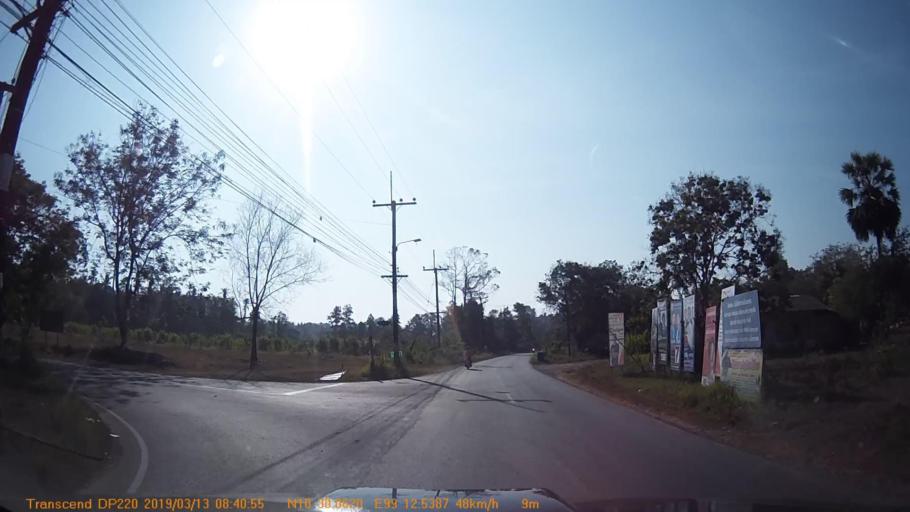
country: TH
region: Chumphon
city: Chumphon
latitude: 10.5009
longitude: 99.2092
